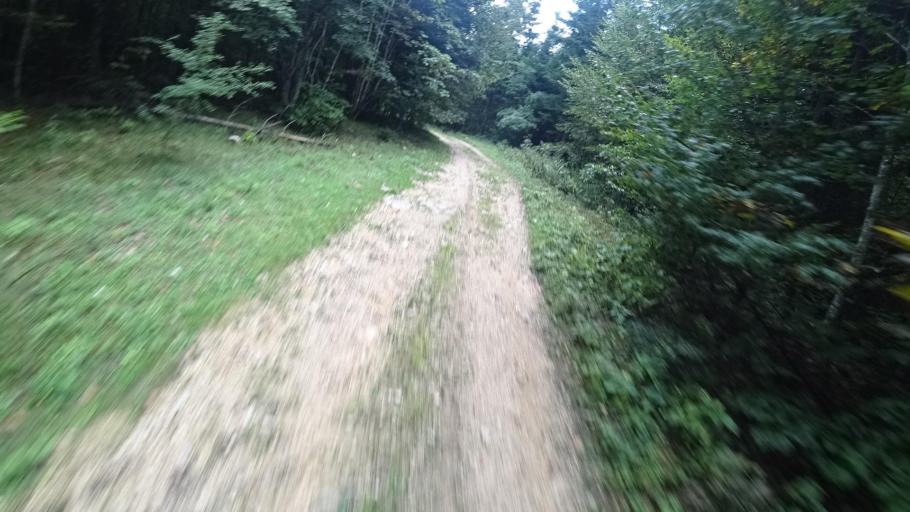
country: BA
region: Republika Srpska
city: Podbrdo
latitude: 44.5940
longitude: 17.0644
